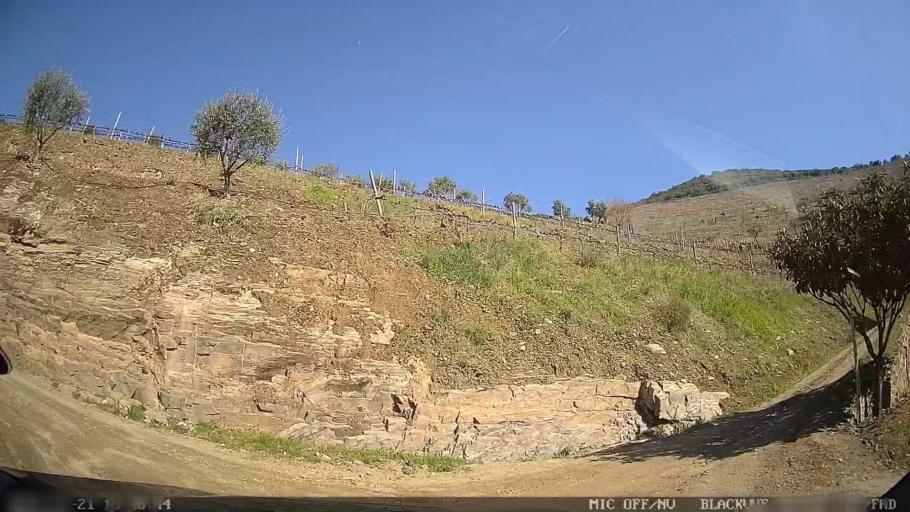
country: PT
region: Viseu
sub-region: Tabuaco
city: Tabuaco
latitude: 41.1758
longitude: -7.5468
